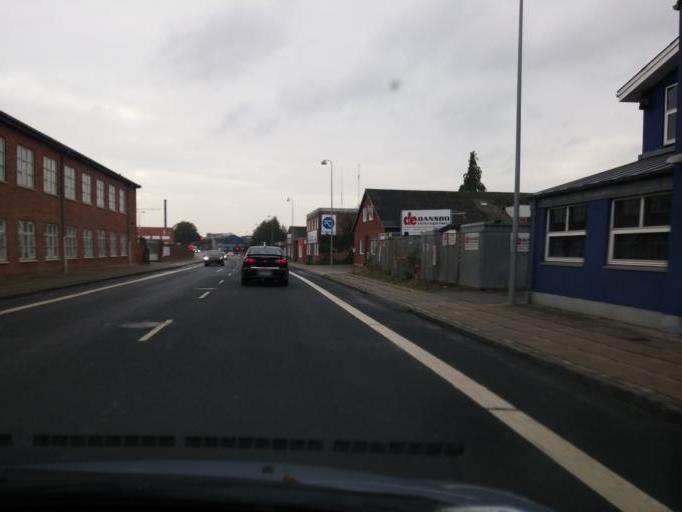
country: DK
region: South Denmark
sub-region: Odense Kommune
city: Odense
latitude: 55.4023
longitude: 10.4045
